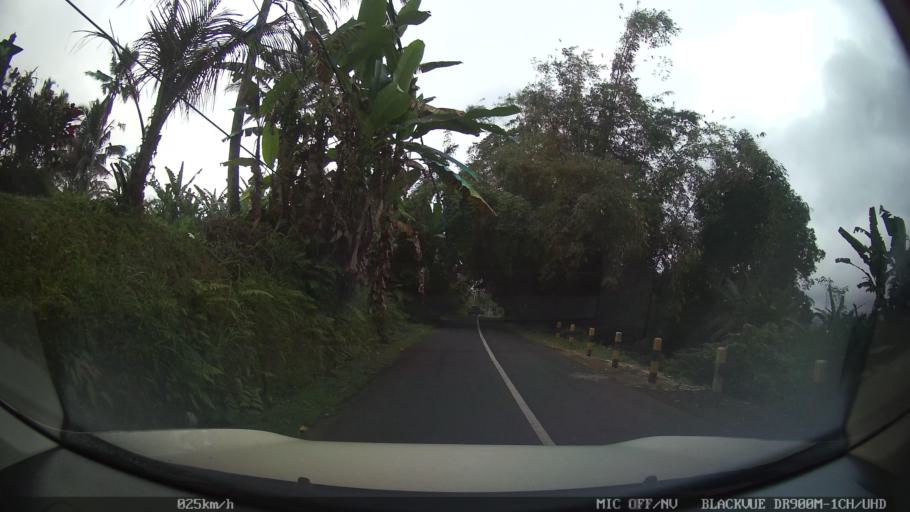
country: ID
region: Bali
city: Peneng
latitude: -8.3435
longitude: 115.1851
